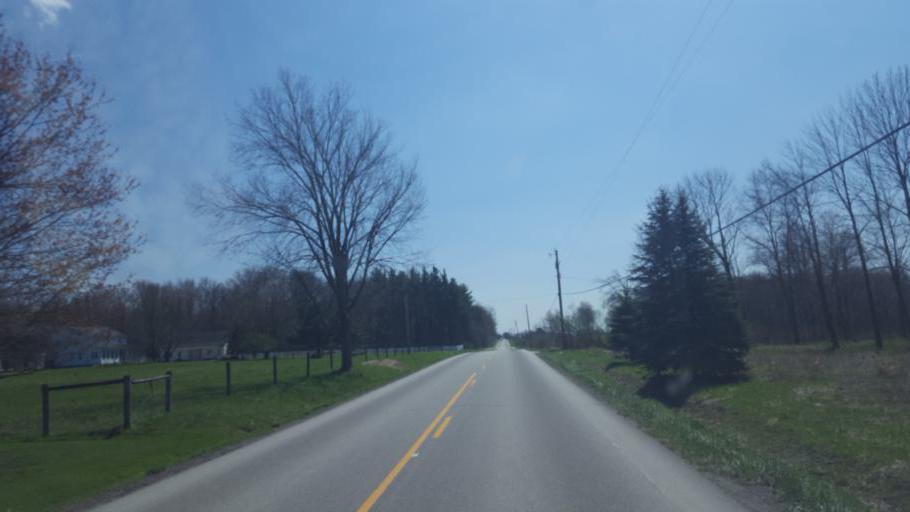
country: US
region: Ohio
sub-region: Geauga County
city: Middlefield
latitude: 41.3934
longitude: -81.1084
